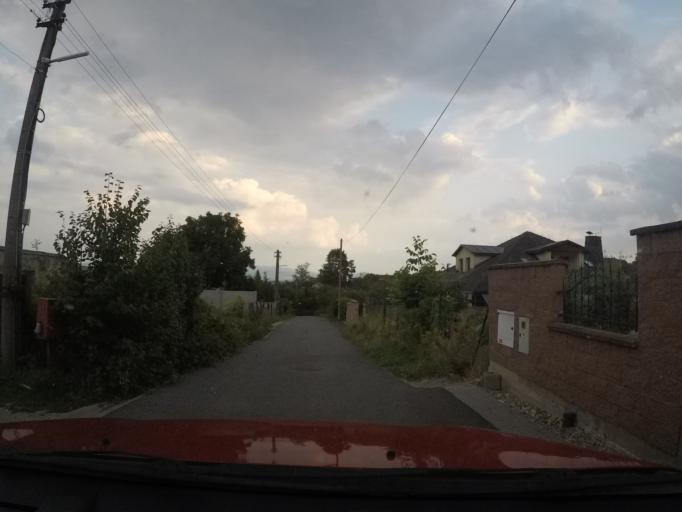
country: SK
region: Kosicky
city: Kosice
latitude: 48.6919
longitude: 21.2126
